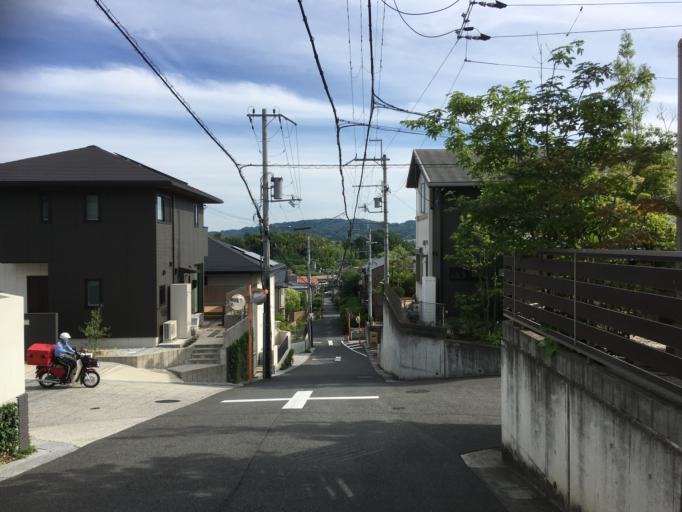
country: JP
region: Nara
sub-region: Ikoma-shi
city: Ikoma
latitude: 34.7002
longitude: 135.7392
